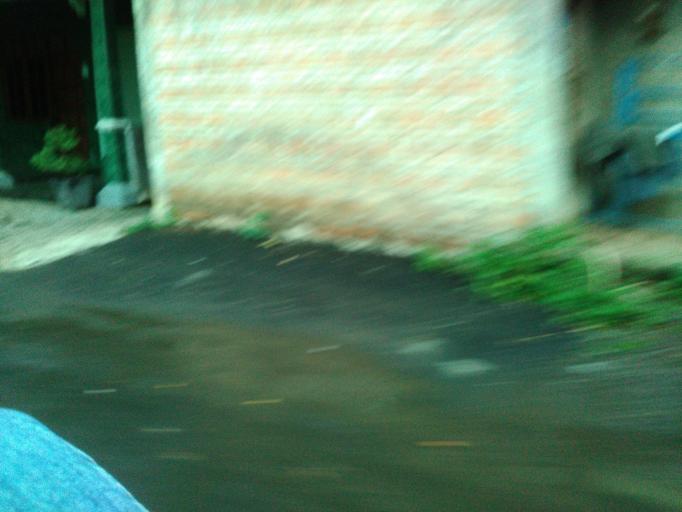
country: ID
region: Central Java
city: Ceper
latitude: -7.6575
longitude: 110.6808
